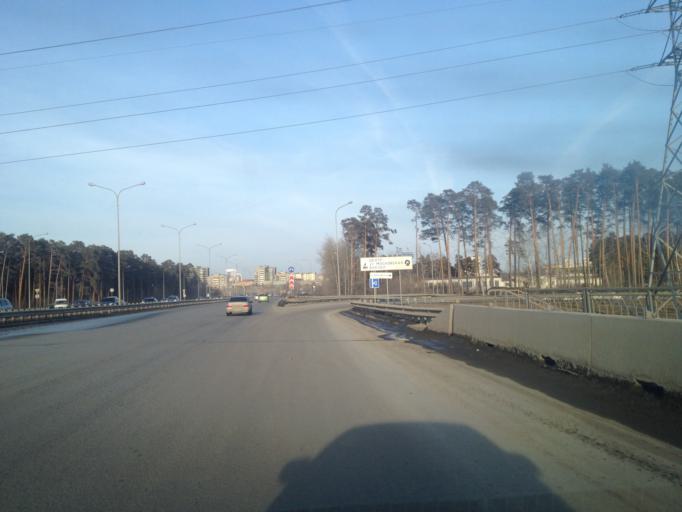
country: RU
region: Sverdlovsk
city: Sovkhoznyy
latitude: 56.7900
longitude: 60.5980
